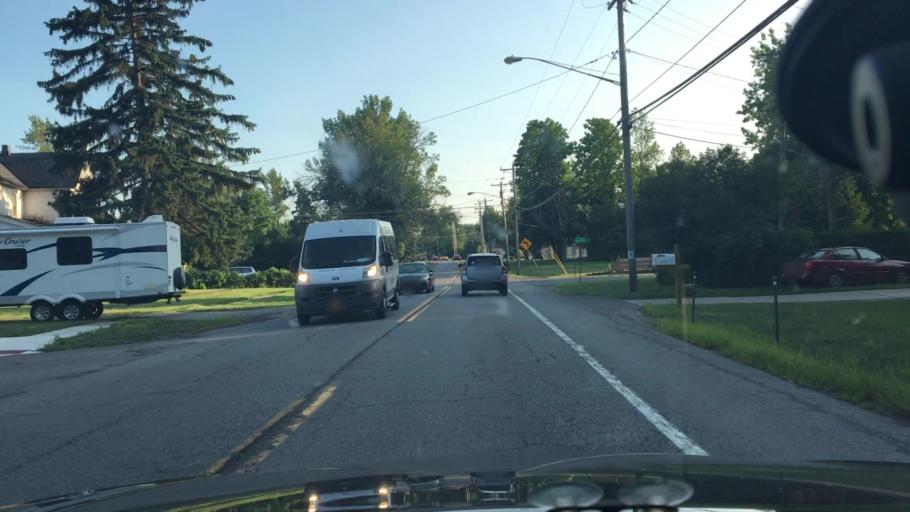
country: US
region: New York
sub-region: Erie County
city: Williamsville
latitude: 42.9866
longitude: -78.7627
